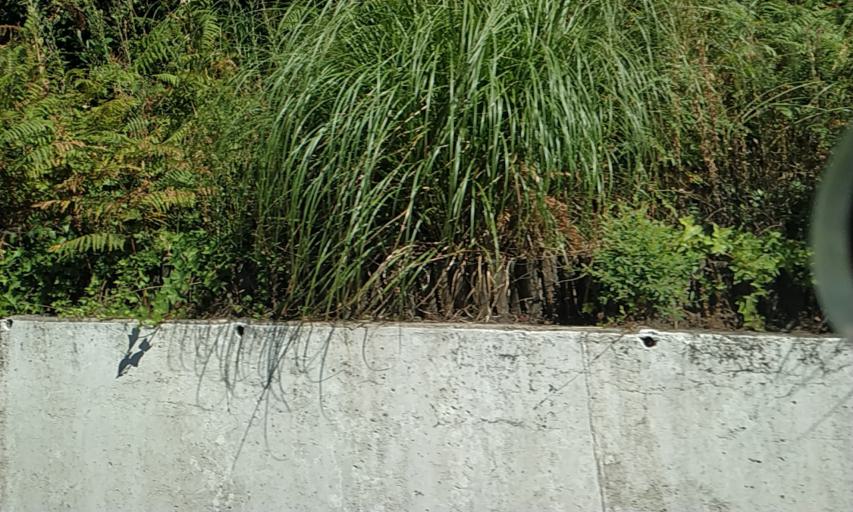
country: PT
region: Porto
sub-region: Trofa
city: Bougado
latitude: 41.3374
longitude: -8.5270
